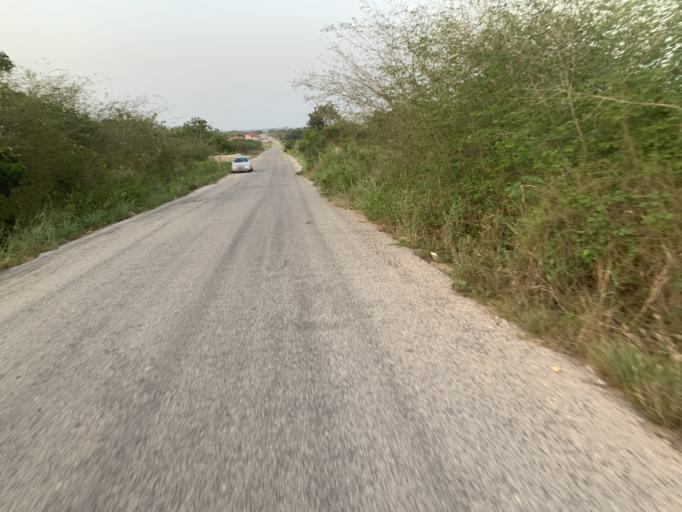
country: GH
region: Central
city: Winneba
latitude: 5.3725
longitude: -0.6149
